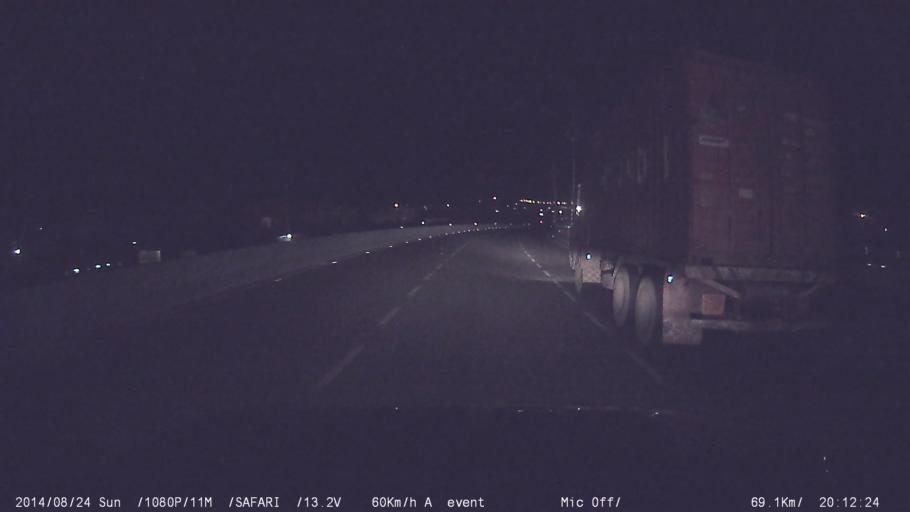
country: IN
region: Tamil Nadu
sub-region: Vellore
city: Vellore
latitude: 12.9267
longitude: 79.1239
